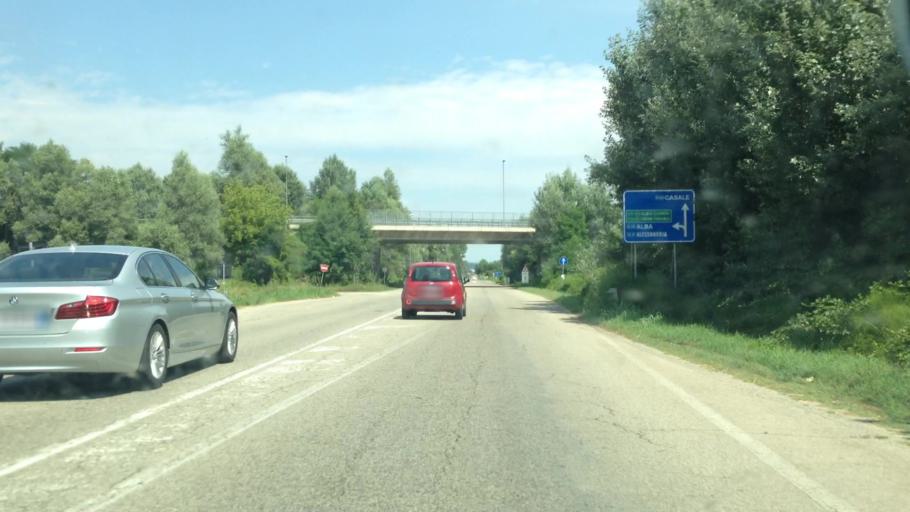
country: IT
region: Piedmont
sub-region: Provincia di Asti
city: Asti
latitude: 44.9229
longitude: 8.2262
